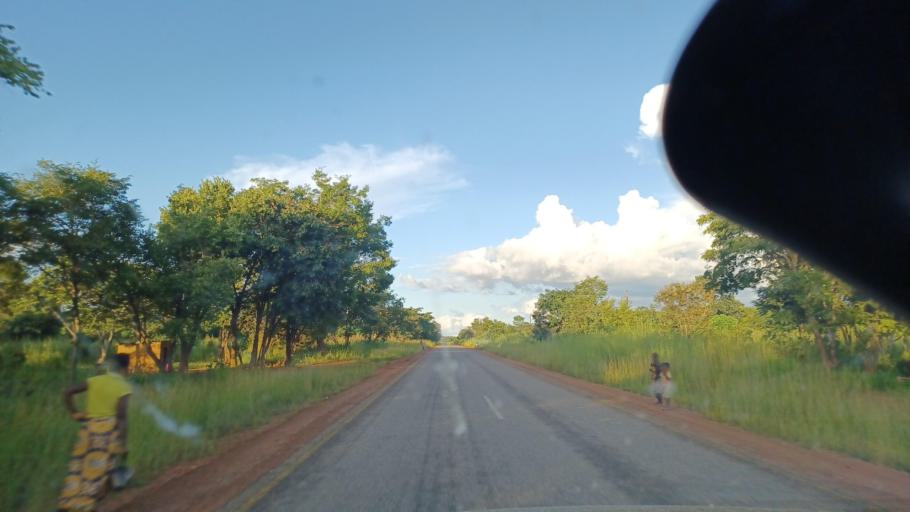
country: ZM
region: North-Western
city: Kalengwa
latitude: -13.1361
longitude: 25.1605
